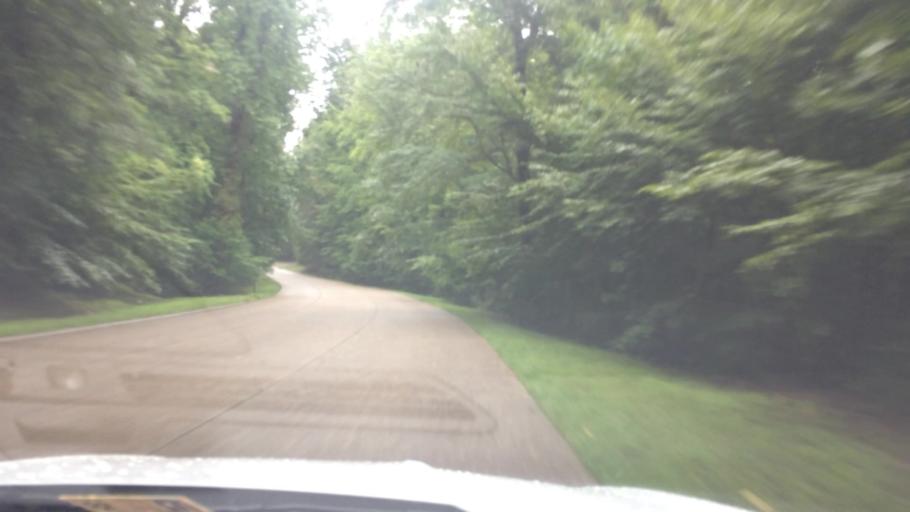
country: US
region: Virginia
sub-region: City of Williamsburg
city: Williamsburg
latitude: 37.2807
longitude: -76.6595
